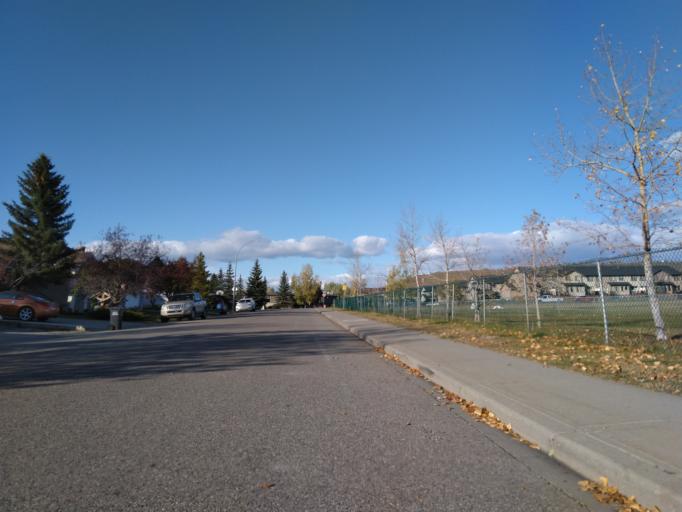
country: CA
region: Alberta
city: Cochrane
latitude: 51.1759
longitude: -114.4691
